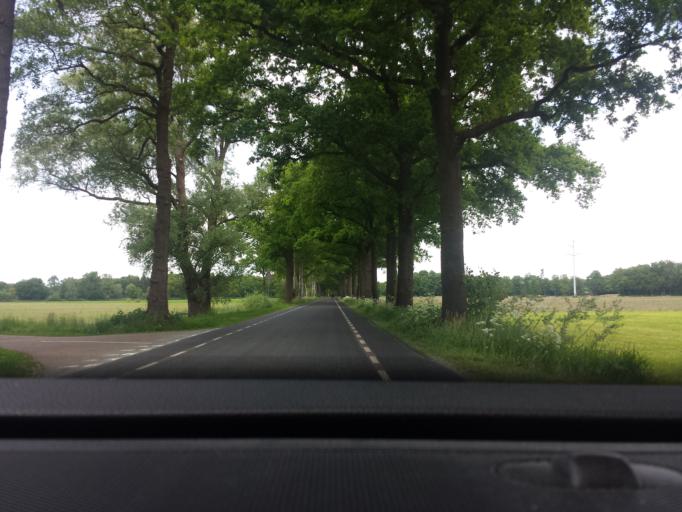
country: NL
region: Gelderland
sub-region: Berkelland
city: Neede
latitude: 52.0919
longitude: 6.5801
